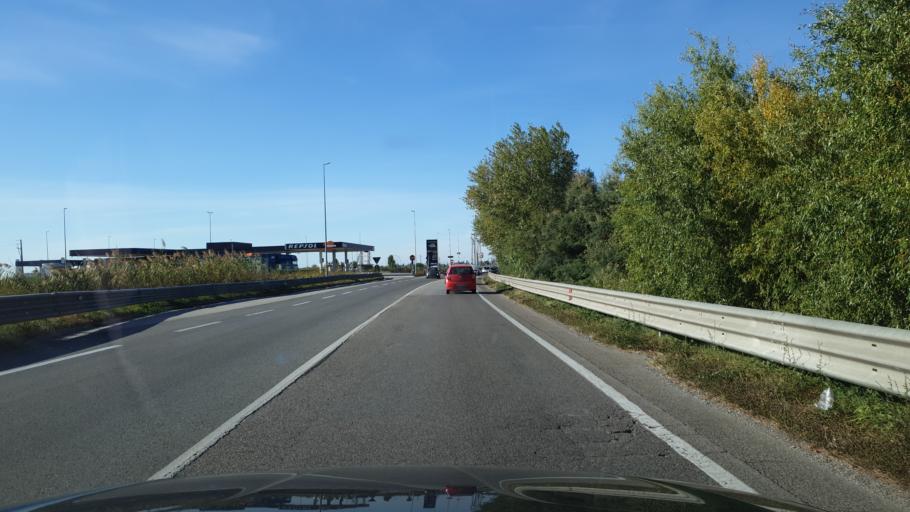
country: IT
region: Emilia-Romagna
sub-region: Provincia di Ravenna
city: Savio
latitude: 44.3087
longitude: 12.2860
